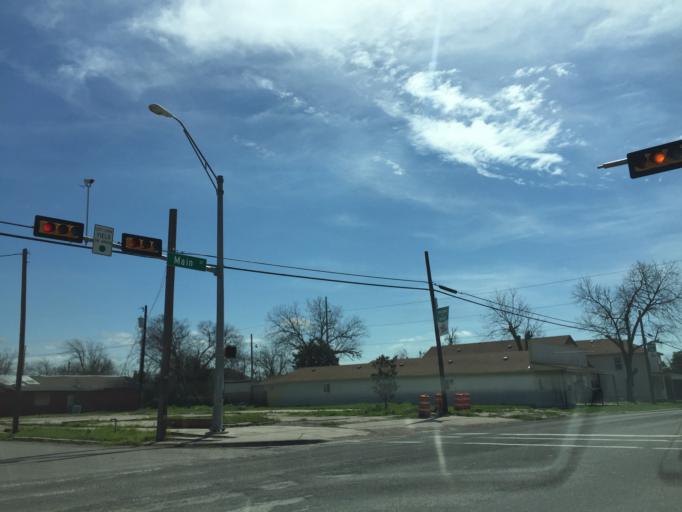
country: US
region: Texas
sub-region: Williamson County
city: Taylor
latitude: 30.5648
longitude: -97.4092
